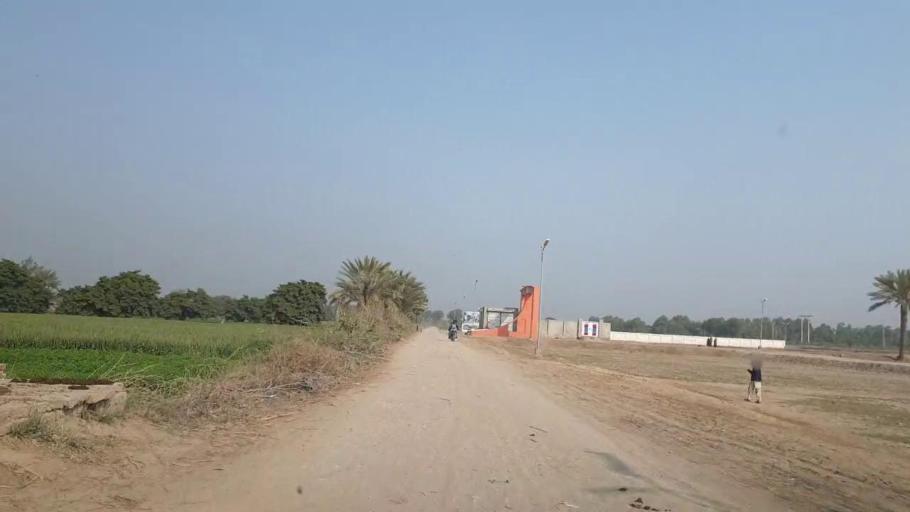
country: PK
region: Sindh
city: Mirpur Khas
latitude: 25.5499
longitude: 69.0195
